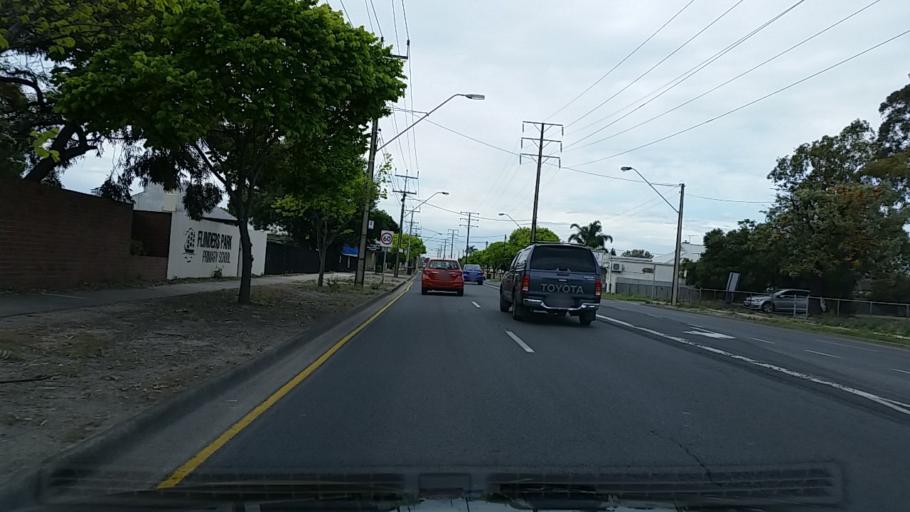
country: AU
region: South Australia
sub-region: Charles Sturt
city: Allenby Gardens
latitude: -34.9114
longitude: 138.5487
